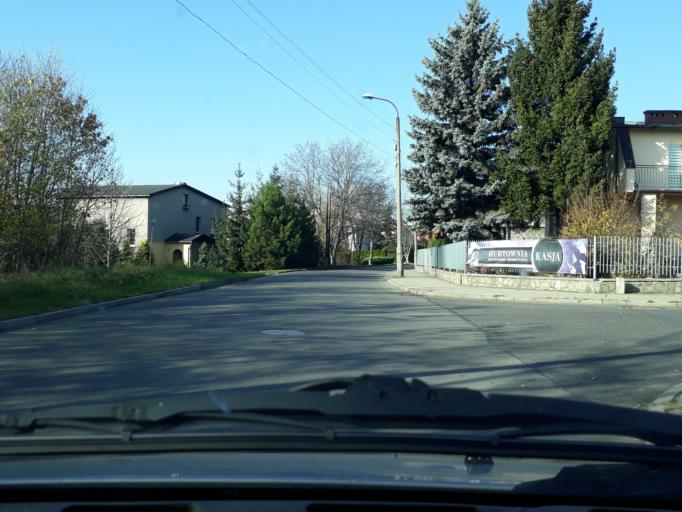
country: PL
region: Silesian Voivodeship
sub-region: Powiat tarnogorski
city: Tarnowskie Gory
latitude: 50.4246
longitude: 18.8752
